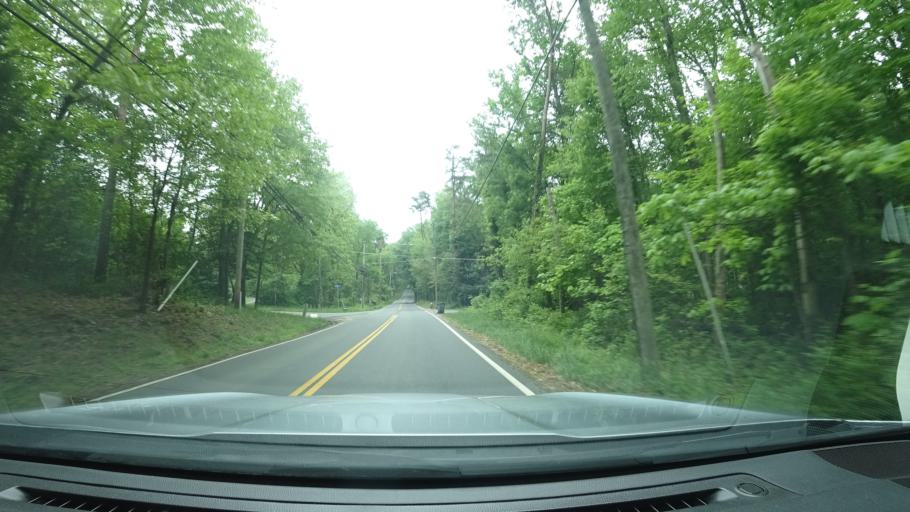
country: US
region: Virginia
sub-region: Fairfax County
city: Oakton
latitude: 38.8860
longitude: -77.3426
